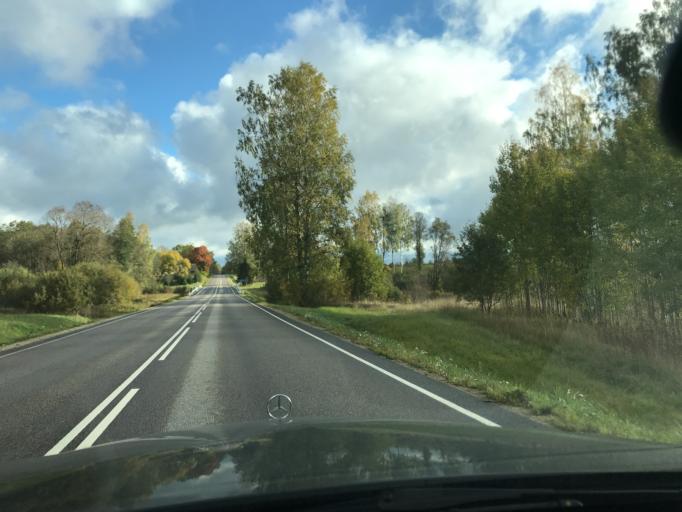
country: EE
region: Valgamaa
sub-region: Torva linn
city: Torva
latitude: 58.0244
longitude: 25.8222
